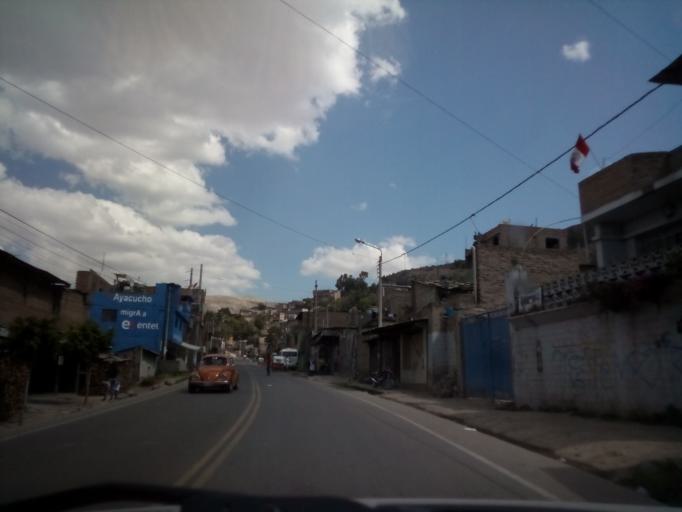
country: PE
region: Ayacucho
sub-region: Provincia de Huamanga
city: Ayacucho
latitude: -13.1535
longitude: -74.2345
